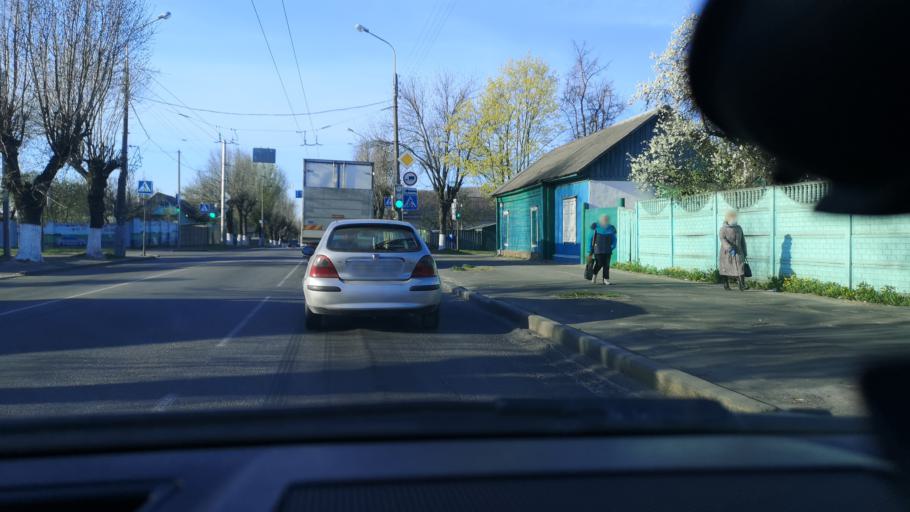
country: BY
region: Gomel
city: Gomel
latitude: 52.4279
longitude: 30.9746
